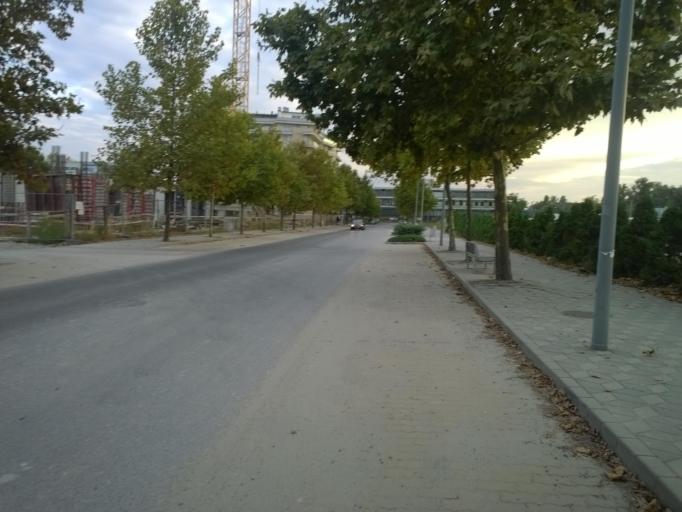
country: HU
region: Budapest
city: Budapest XI. keruelet
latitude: 47.4591
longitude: 19.0483
